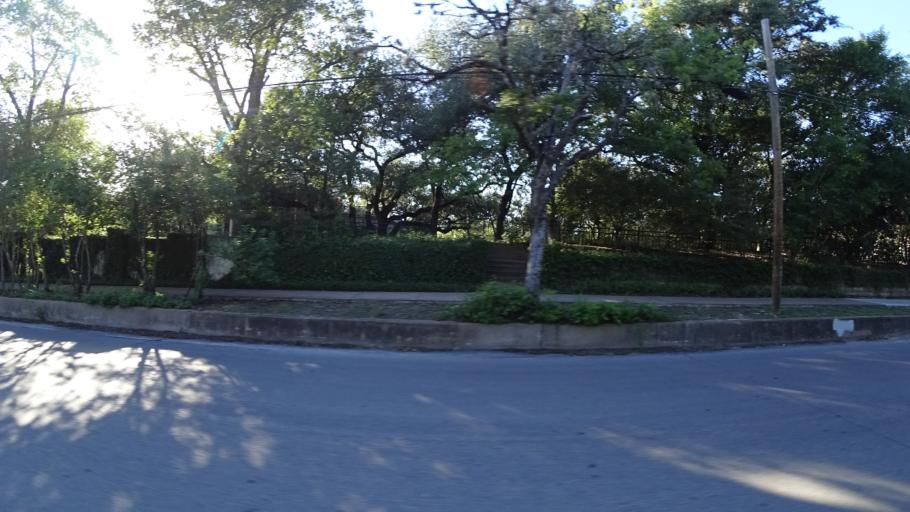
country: US
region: Texas
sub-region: Travis County
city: Austin
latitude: 30.2942
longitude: -97.7326
